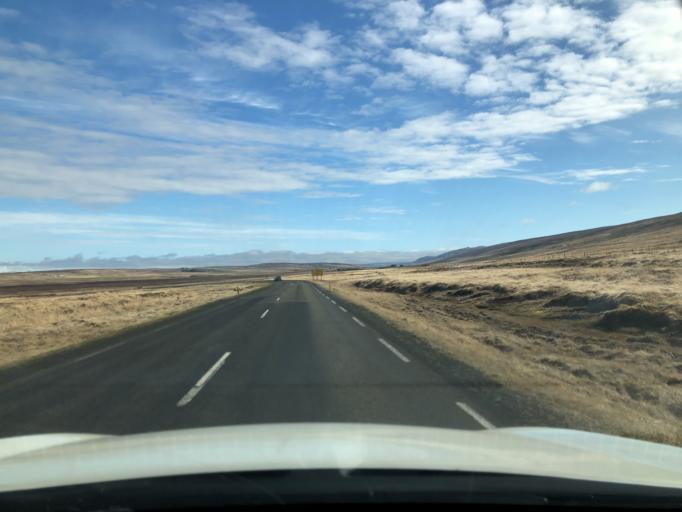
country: IS
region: West
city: Borgarnes
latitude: 65.0871
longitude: -21.7481
